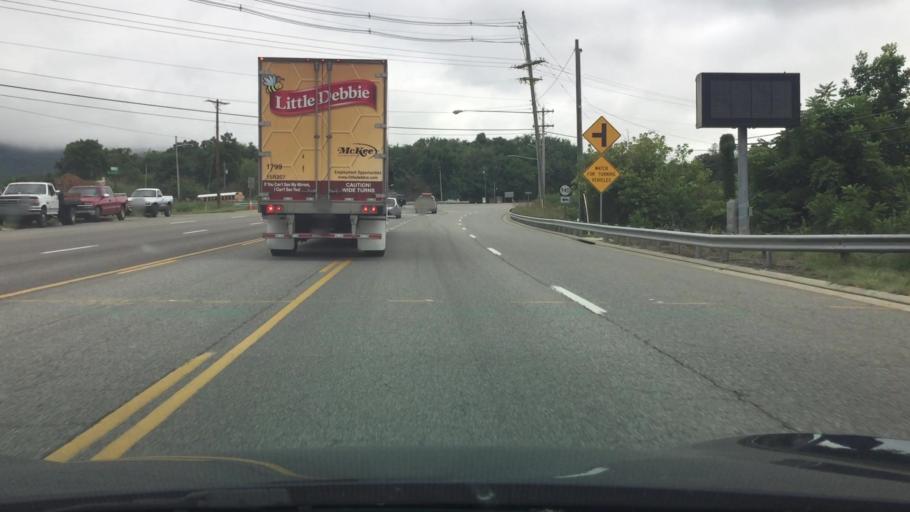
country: US
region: Virginia
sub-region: Montgomery County
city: Shawsville
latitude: 37.2535
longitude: -80.1738
